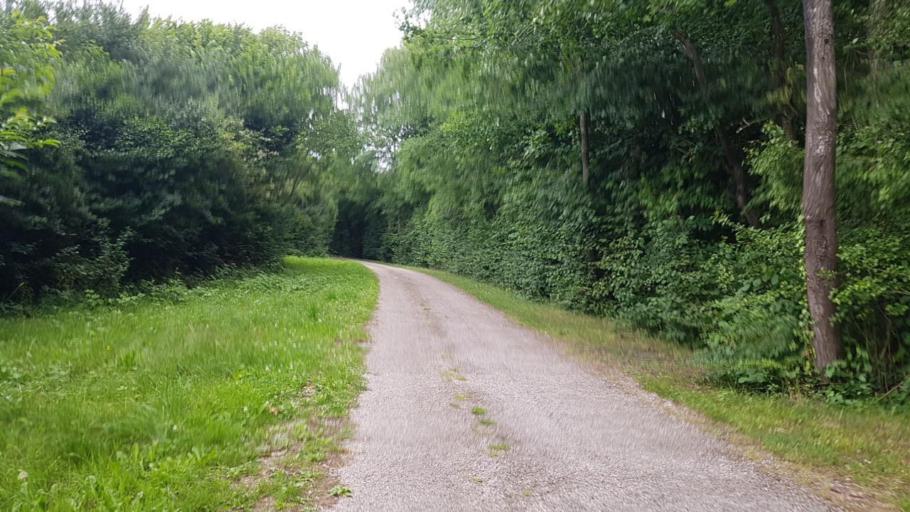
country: FR
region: Picardie
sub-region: Departement de l'Aisne
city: Origny-en-Thierache
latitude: 49.9274
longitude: 3.9908
